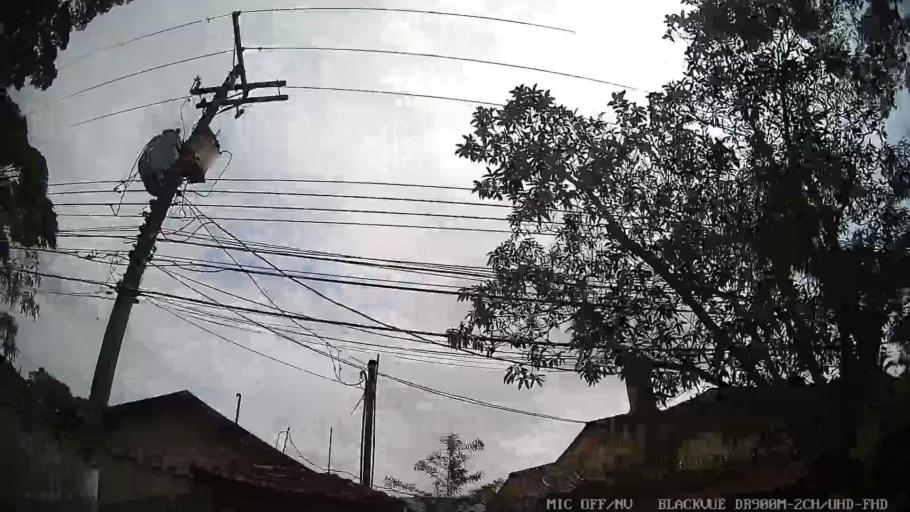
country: BR
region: Sao Paulo
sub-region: Diadema
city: Diadema
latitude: -23.6314
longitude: -46.6769
